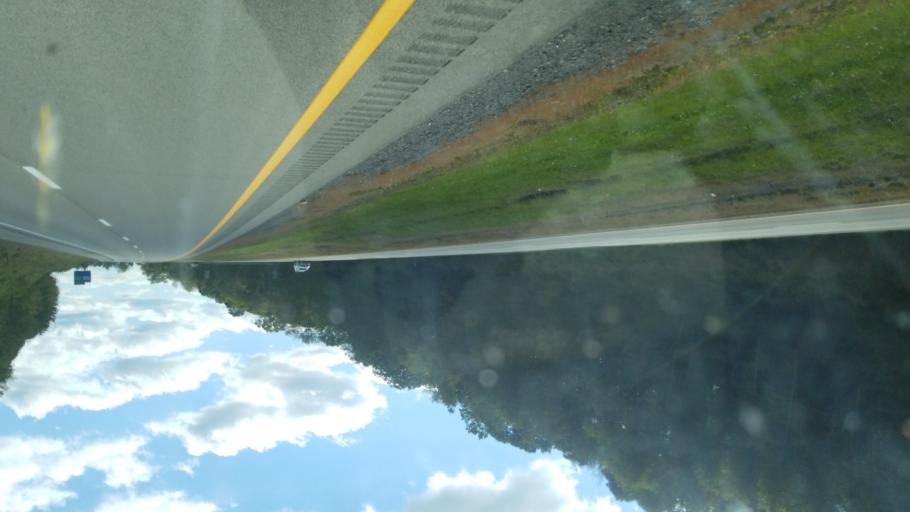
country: US
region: West Virginia
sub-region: Preston County
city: Kingwood
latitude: 39.6618
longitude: -79.6036
